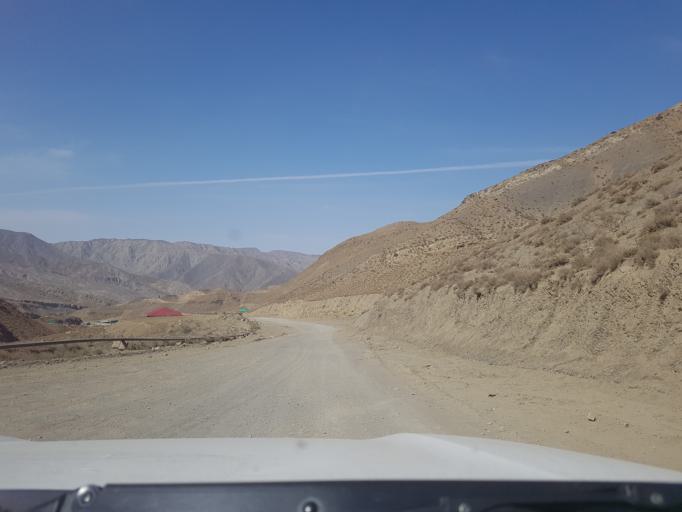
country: TM
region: Ahal
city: Baharly
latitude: 38.4474
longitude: 57.0480
